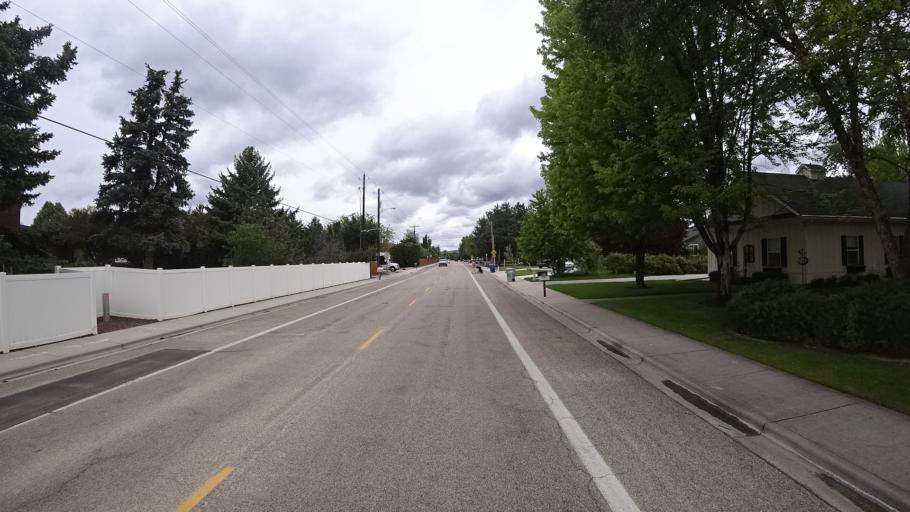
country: US
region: Idaho
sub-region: Ada County
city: Eagle
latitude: 43.7021
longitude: -116.3341
